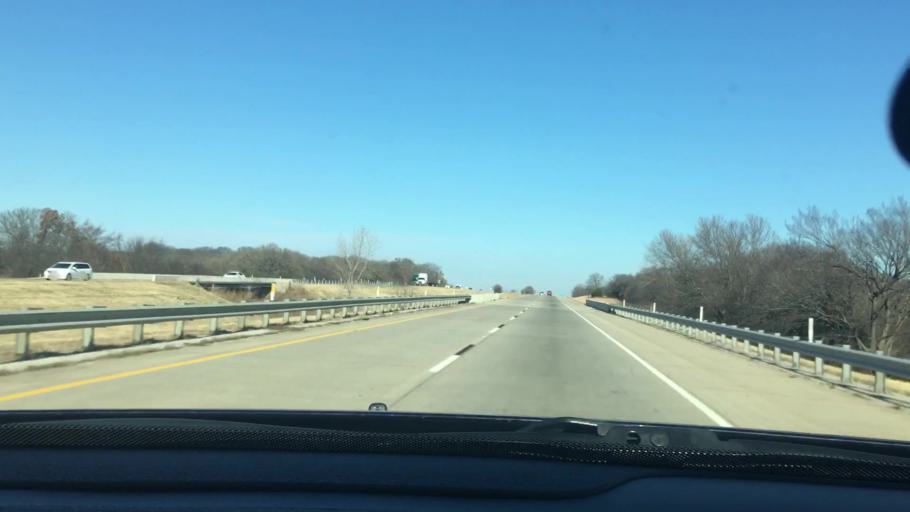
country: US
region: Oklahoma
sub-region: Love County
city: Marietta
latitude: 34.0121
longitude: -97.1431
